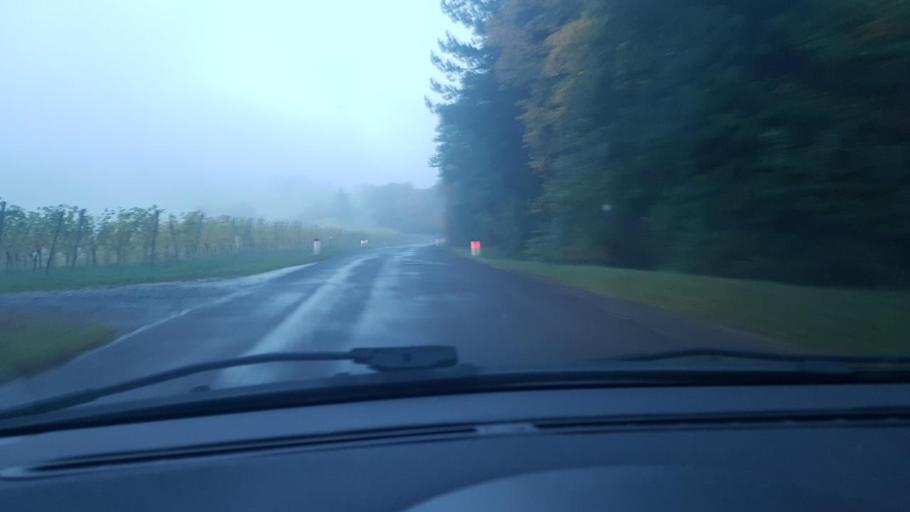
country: AT
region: Styria
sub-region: Politischer Bezirk Leibnitz
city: Sulztal an der Weinstrasse
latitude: 46.6679
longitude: 15.5383
